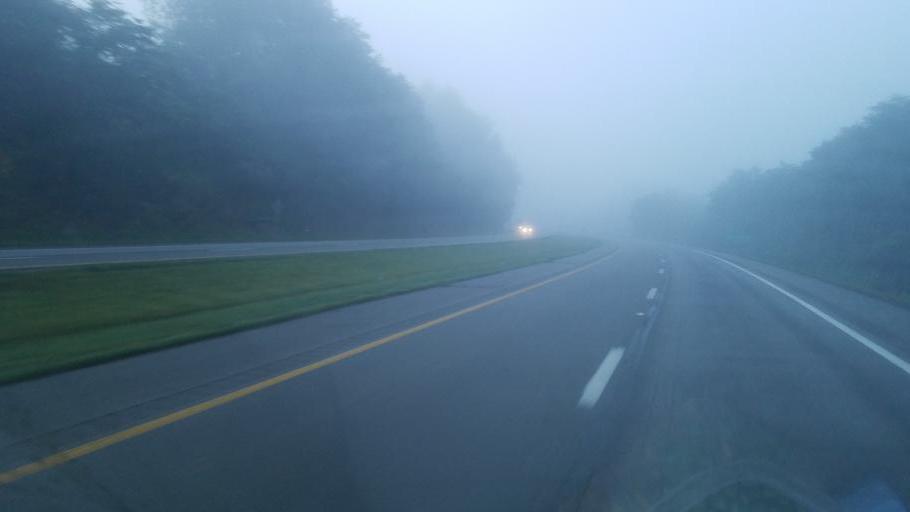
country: US
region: Ohio
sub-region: Jackson County
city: Jackson
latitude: 39.1346
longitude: -82.7157
